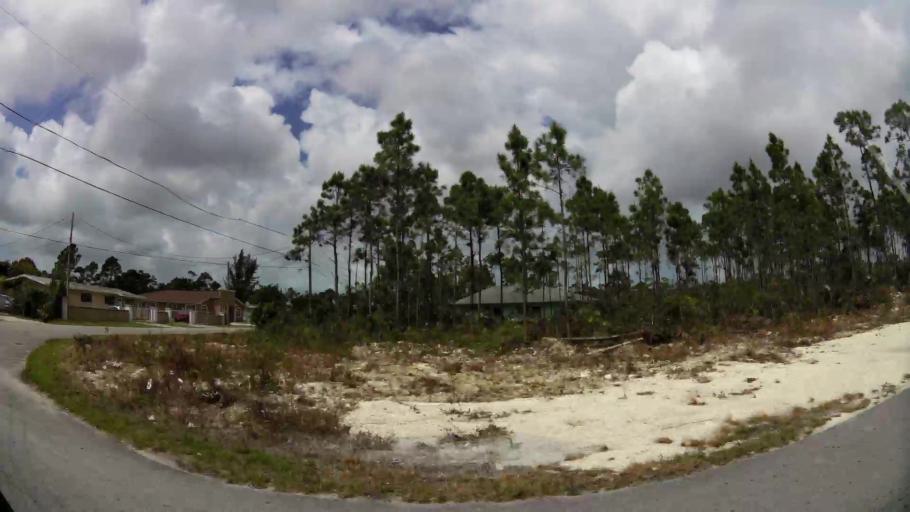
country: BS
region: Freeport
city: Lucaya
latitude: 26.5437
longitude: -78.6463
